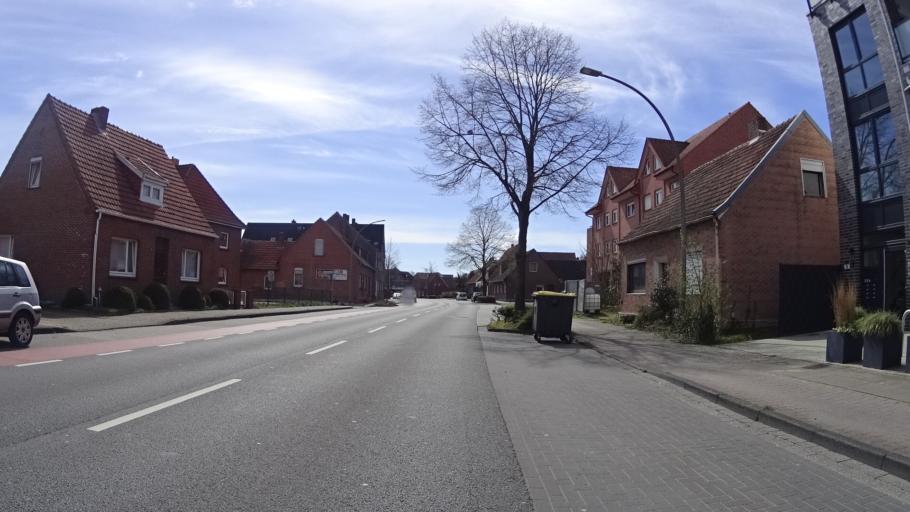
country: DE
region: Lower Saxony
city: Lingen
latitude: 52.5100
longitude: 7.3186
